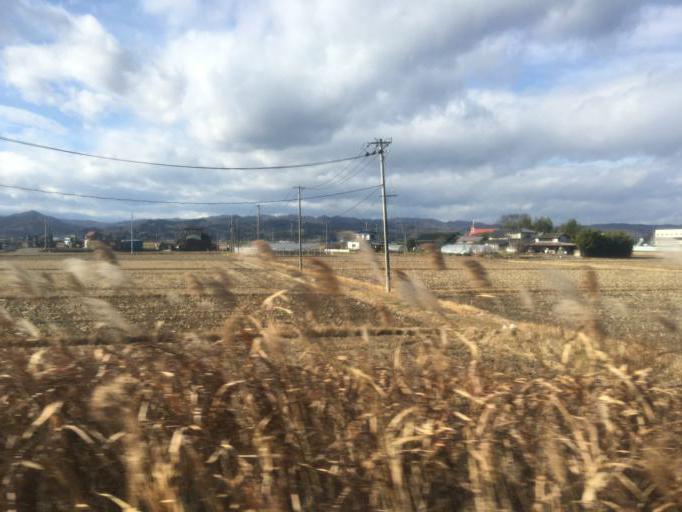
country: JP
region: Miyagi
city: Iwanuma
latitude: 38.1338
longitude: 140.8759
